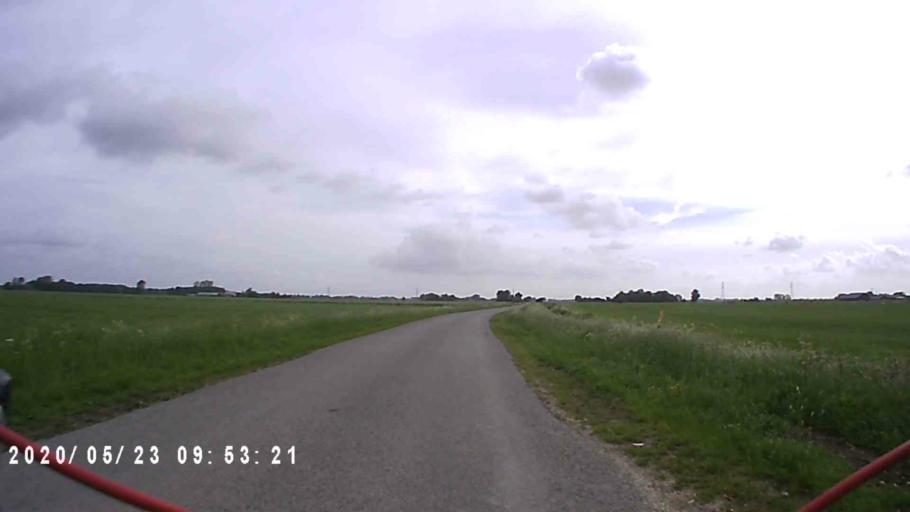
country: NL
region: Groningen
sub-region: Gemeente Appingedam
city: Appingedam
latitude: 53.2989
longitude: 6.7904
